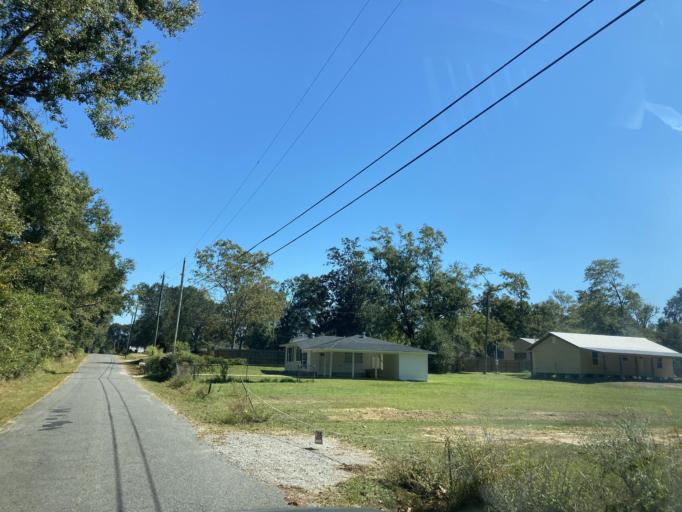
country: US
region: Mississippi
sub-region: Jackson County
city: Saint Martin
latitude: 30.4721
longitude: -88.8782
